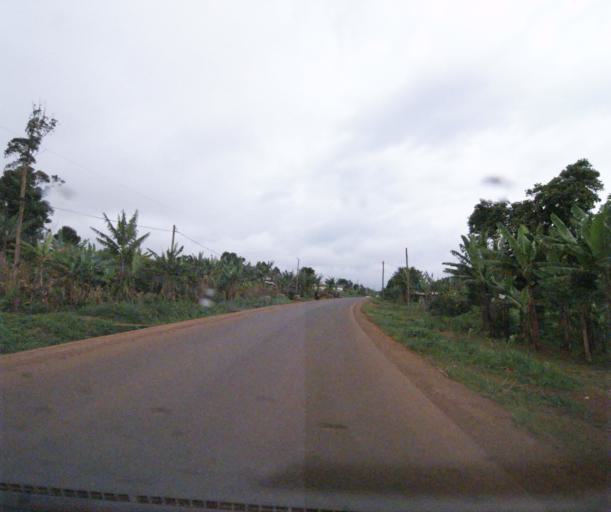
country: CM
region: West
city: Dschang
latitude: 5.4962
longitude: 10.1581
